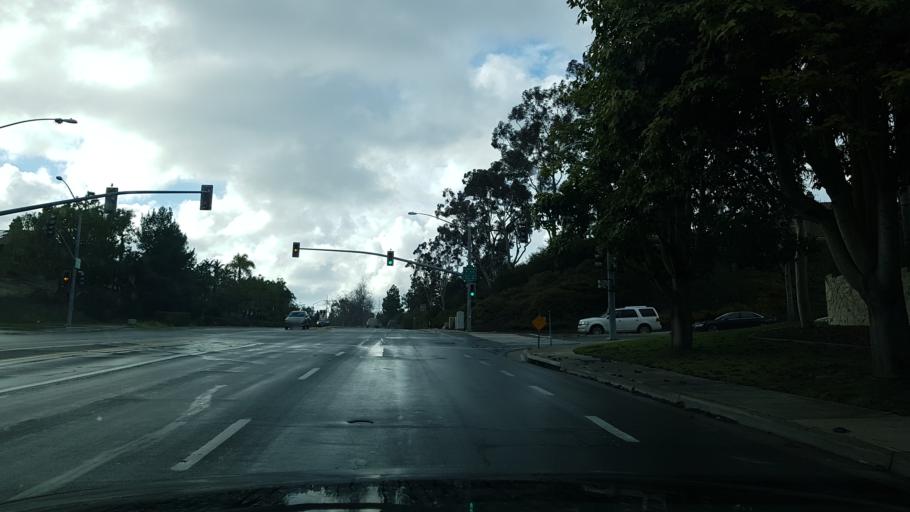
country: US
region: California
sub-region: San Diego County
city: Del Mar
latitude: 32.9451
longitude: -117.2163
